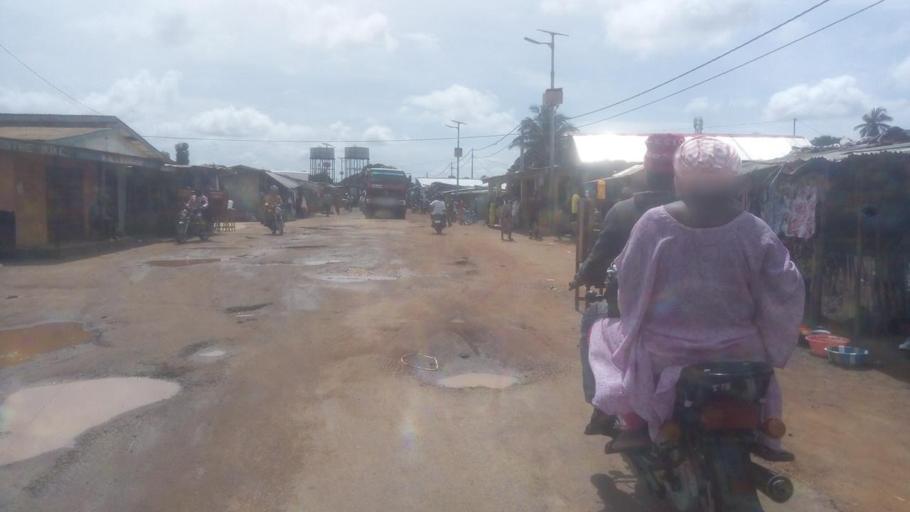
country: SL
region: Northern Province
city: Masoyila
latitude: 8.6025
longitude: -13.1819
